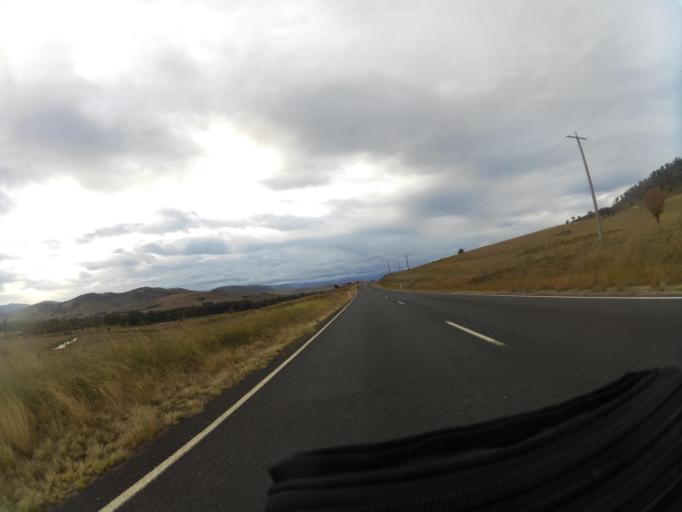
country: AU
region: New South Wales
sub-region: Snowy River
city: Jindabyne
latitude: -36.0794
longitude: 147.9741
